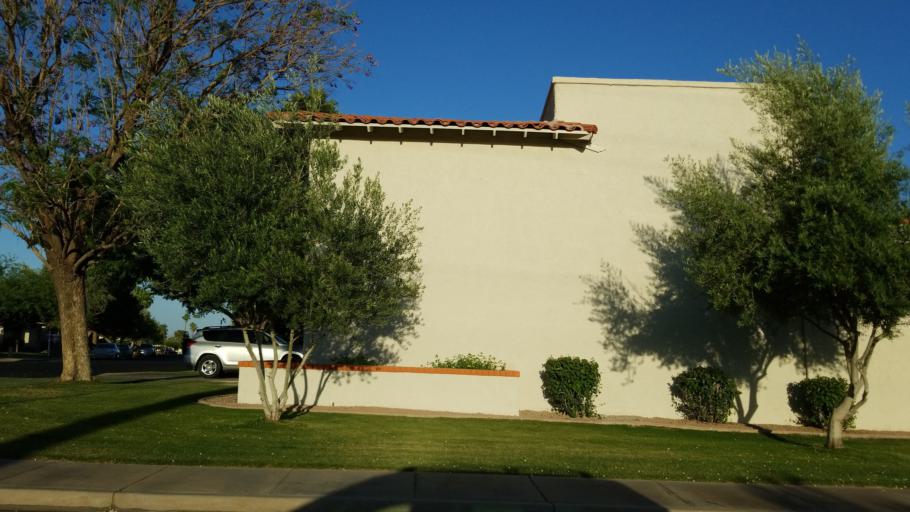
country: US
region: Arizona
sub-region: Maricopa County
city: Scottsdale
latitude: 33.5133
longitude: -111.9172
